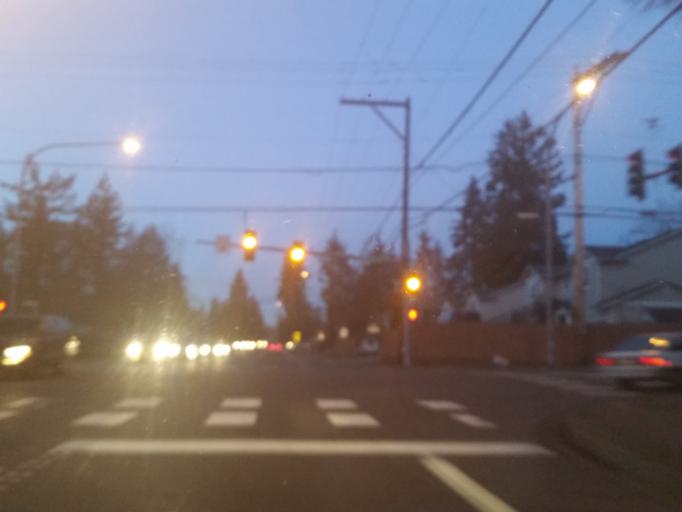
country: US
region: Washington
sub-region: Snohomish County
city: Meadowdale
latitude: 47.8643
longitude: -122.3036
